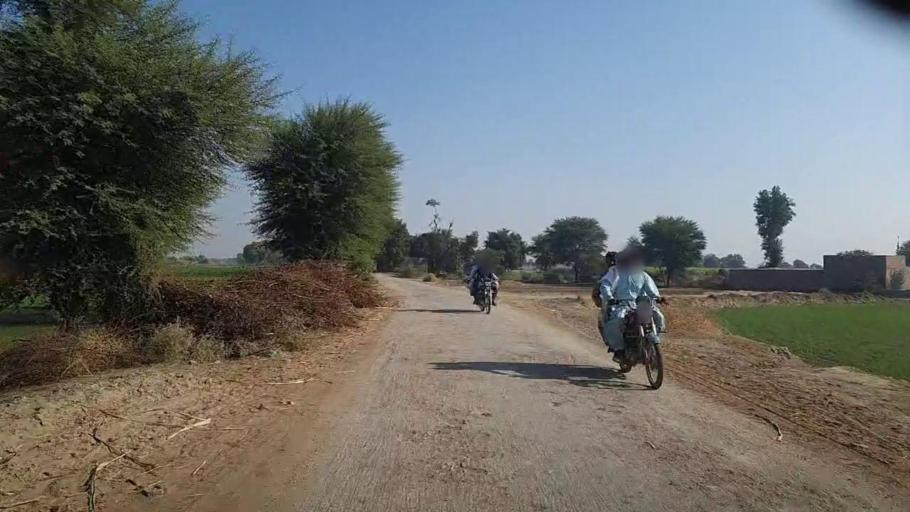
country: PK
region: Sindh
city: Darya Khan Marri
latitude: 26.6580
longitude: 68.3471
